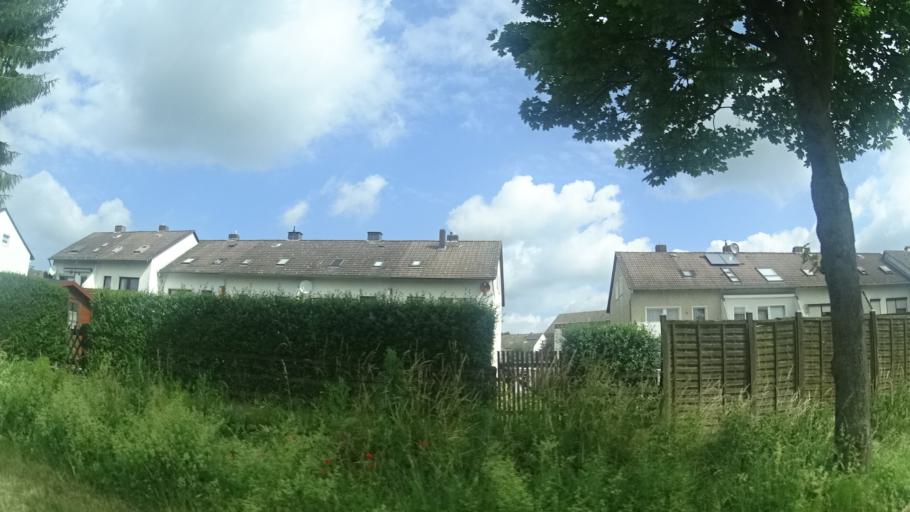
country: DE
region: Lower Saxony
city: Ronnenberg
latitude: 52.2394
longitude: 9.6519
